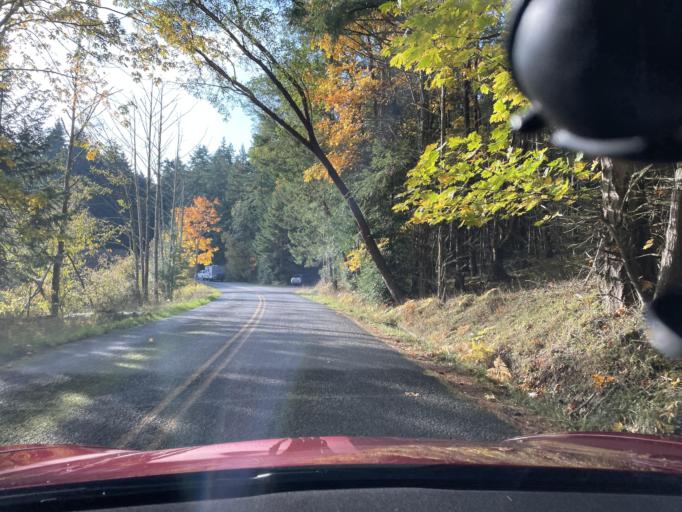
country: US
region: Washington
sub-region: San Juan County
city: Friday Harbor
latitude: 48.5236
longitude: -123.1458
